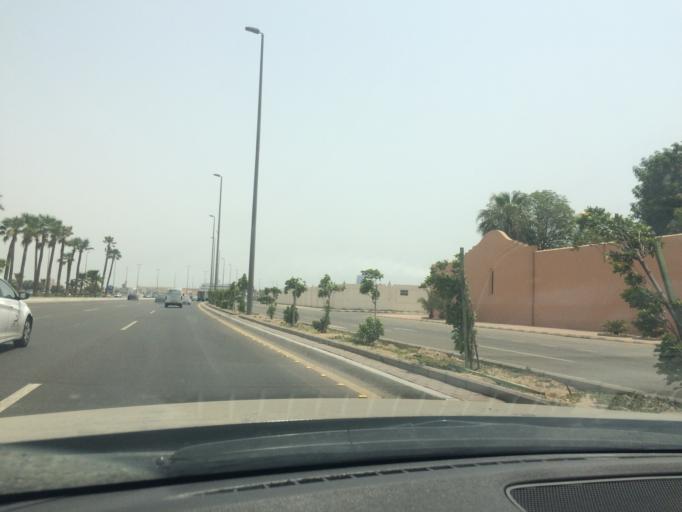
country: SA
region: Makkah
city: Jeddah
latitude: 21.5846
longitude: 39.1260
